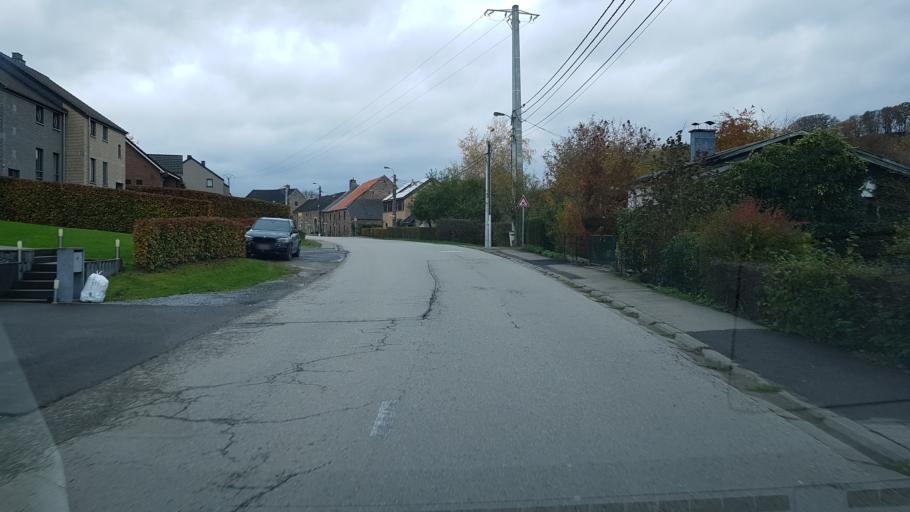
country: BE
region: Wallonia
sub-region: Province de Liege
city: Theux
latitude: 50.5051
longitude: 5.8086
